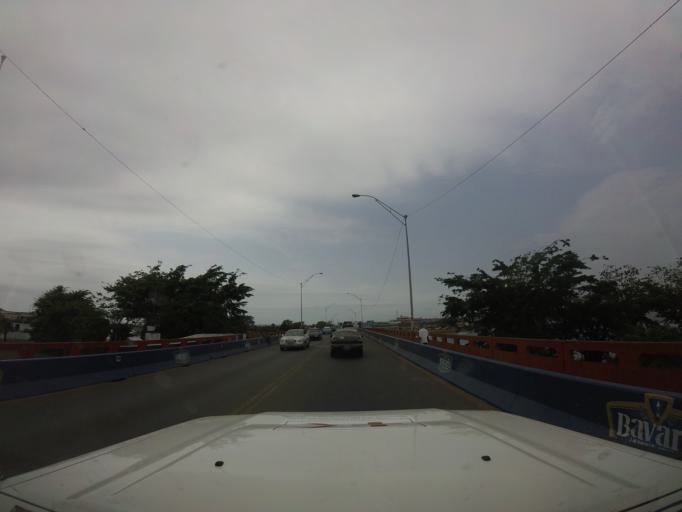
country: LR
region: Montserrado
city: Monrovia
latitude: 6.3199
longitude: -10.8019
